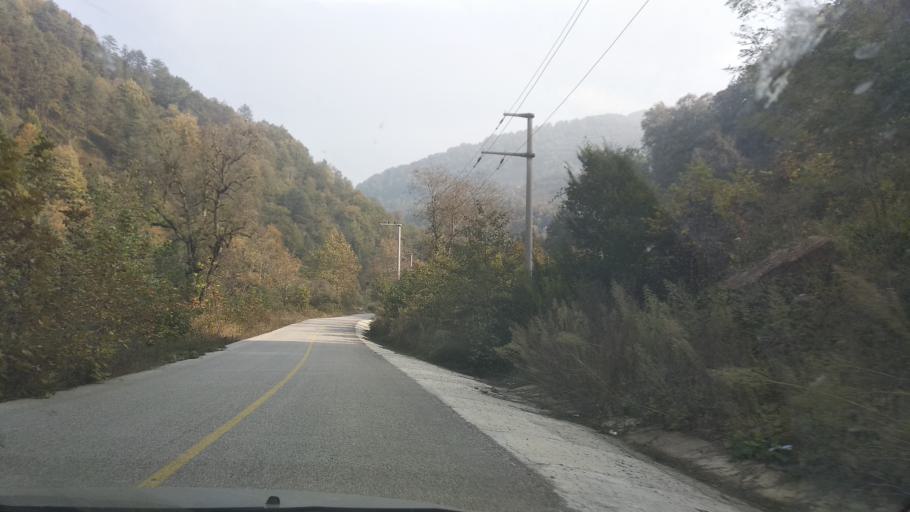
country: TR
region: Duzce
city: Kaynasli
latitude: 40.7280
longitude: 31.2365
